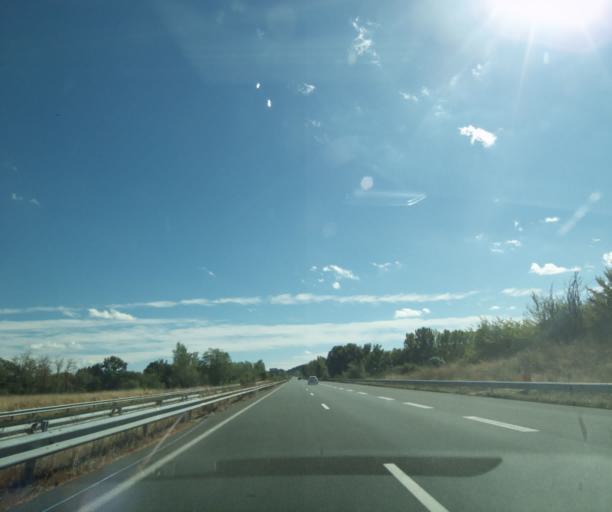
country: FR
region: Aquitaine
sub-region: Departement du Lot-et-Garonne
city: Damazan
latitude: 44.2804
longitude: 0.2696
